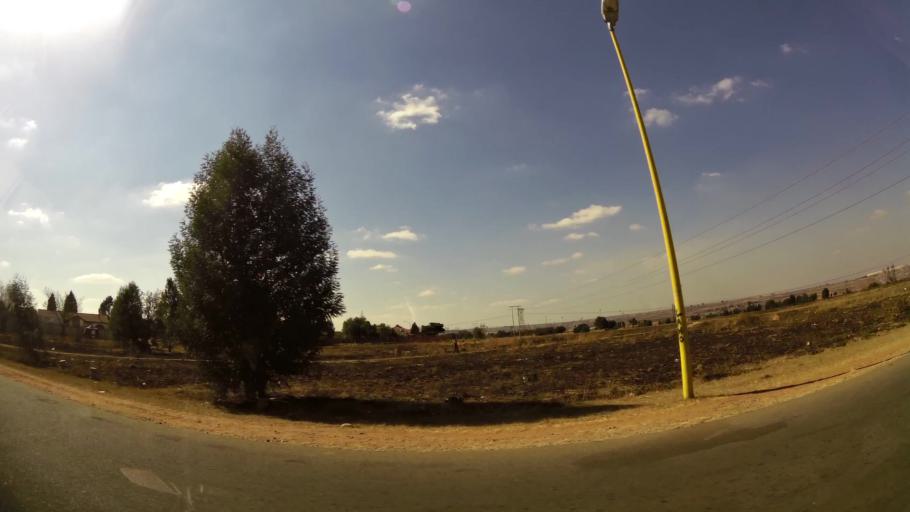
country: ZA
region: Gauteng
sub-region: West Rand District Municipality
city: Randfontein
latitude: -26.1782
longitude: 27.7484
